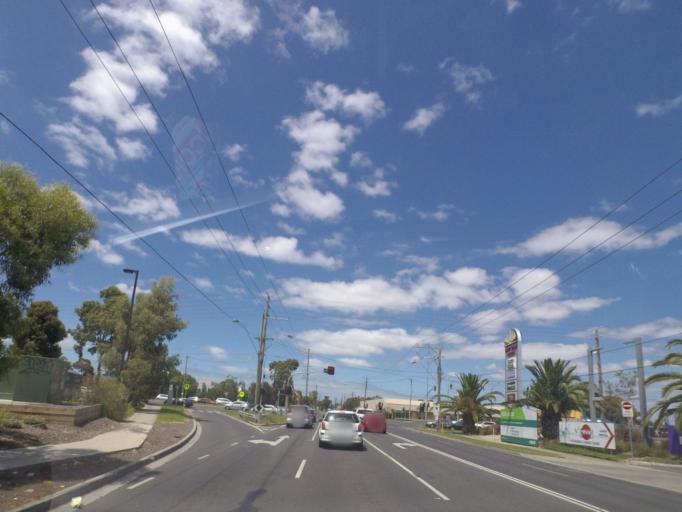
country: AU
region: Victoria
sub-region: Brimbank
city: Sunshine North
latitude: -37.7763
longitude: 144.8288
